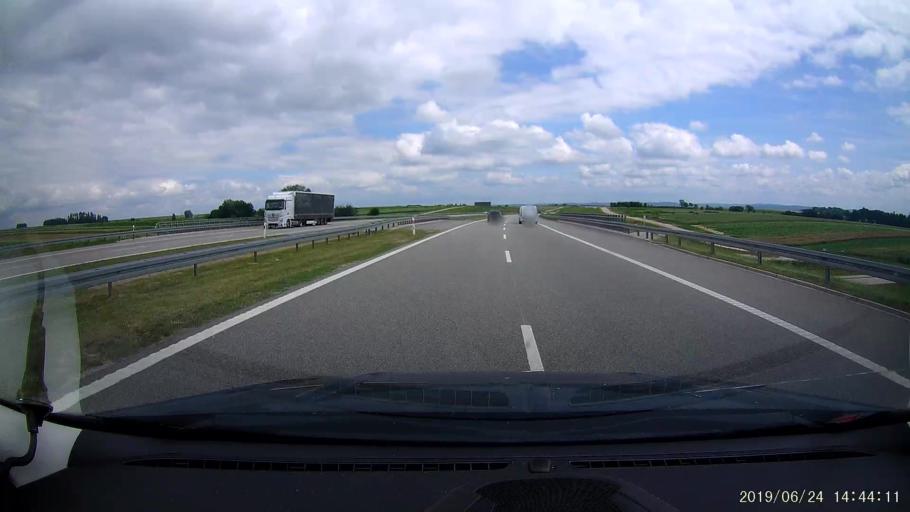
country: PL
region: Subcarpathian Voivodeship
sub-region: Powiat debicki
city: Czarna
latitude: 50.0985
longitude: 21.2847
